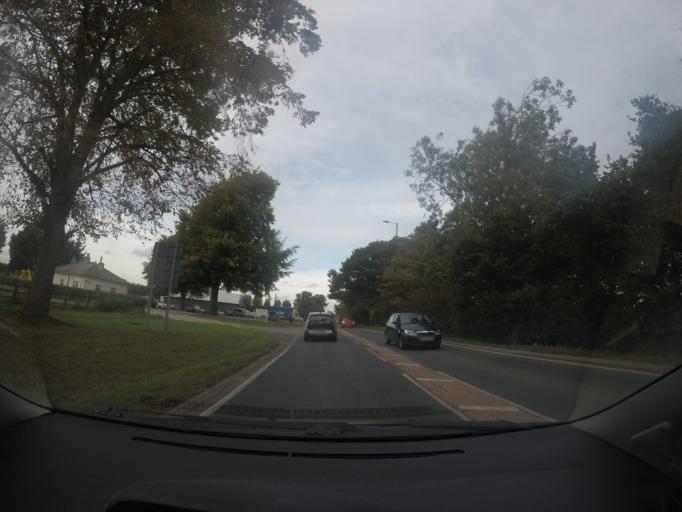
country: GB
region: England
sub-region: City of York
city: Deighton
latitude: 53.9136
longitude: -1.0515
